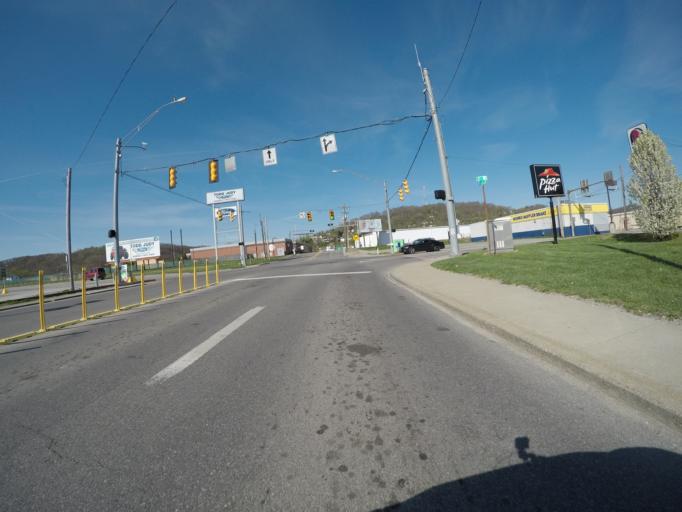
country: US
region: West Virginia
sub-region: Kanawha County
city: South Charleston
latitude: 38.3694
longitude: -81.6664
